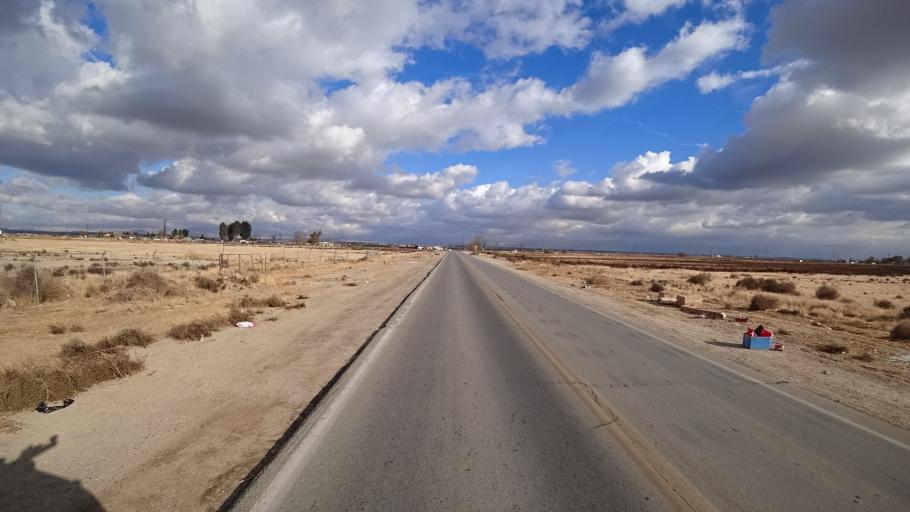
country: US
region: California
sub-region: Kern County
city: Greenfield
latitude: 35.3104
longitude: -118.9884
